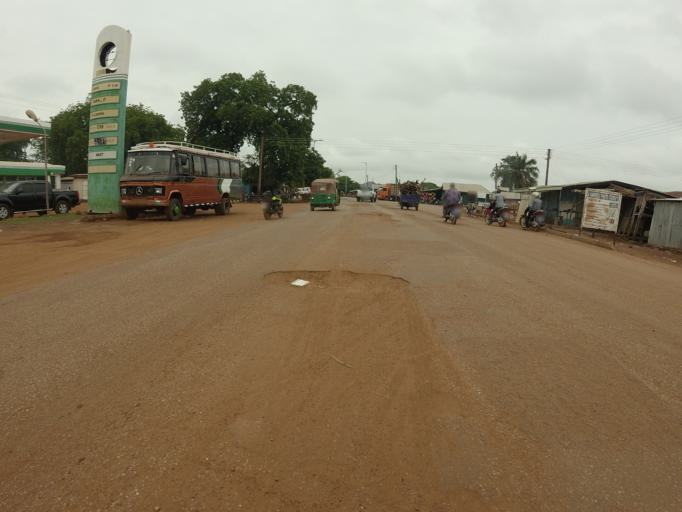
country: GH
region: Northern
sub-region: Yendi
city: Yendi
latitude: 9.4462
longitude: -0.0069
